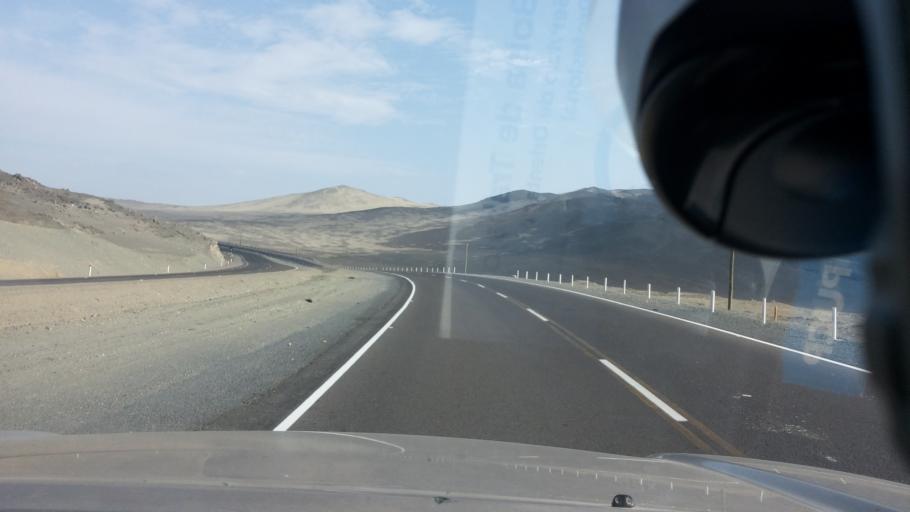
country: PE
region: Ancash
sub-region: Provincia de Huarmey
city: La Caleta Culebras
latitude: -9.7274
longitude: -78.2670
